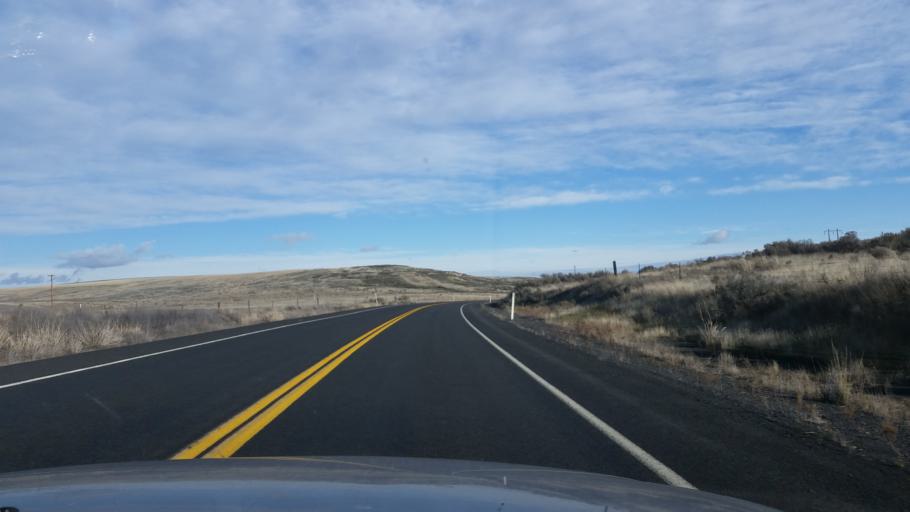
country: US
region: Washington
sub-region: Adams County
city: Ritzville
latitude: 47.3470
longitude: -118.5995
